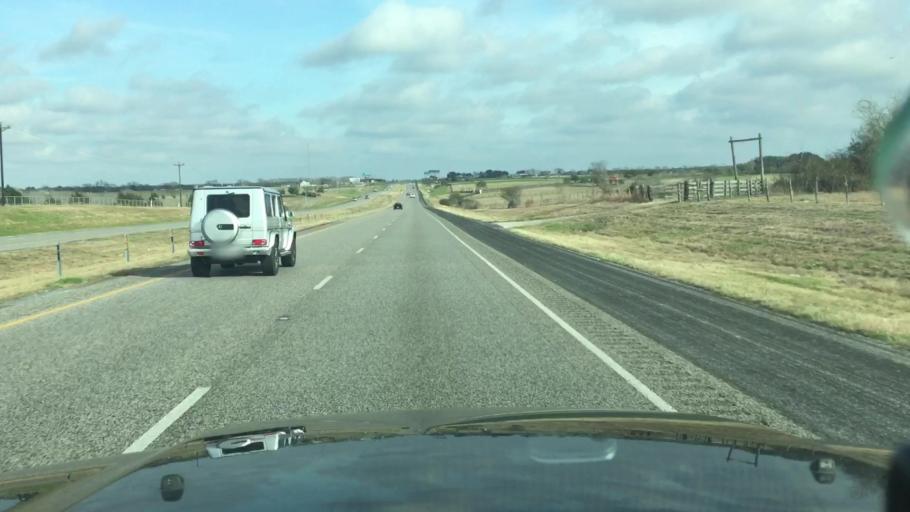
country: US
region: Texas
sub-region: Washington County
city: Brenham
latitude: 30.1391
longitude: -96.3114
